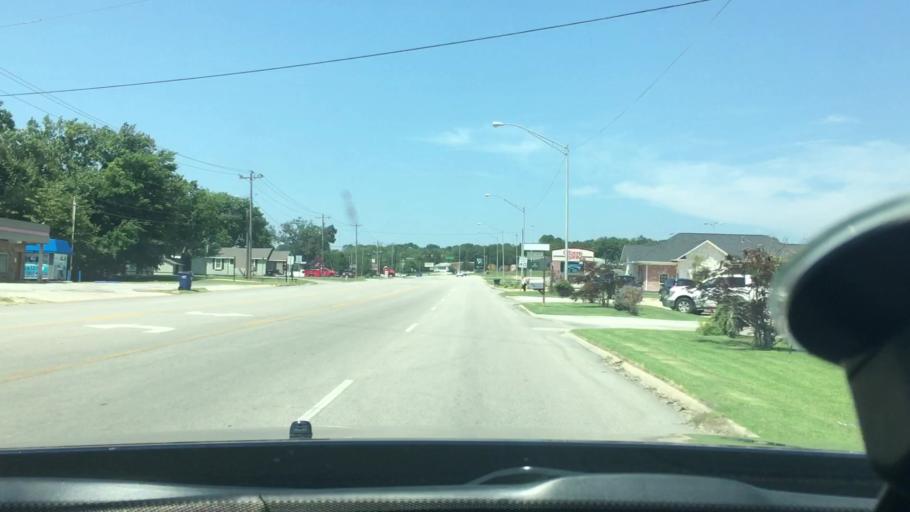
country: US
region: Oklahoma
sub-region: Pontotoc County
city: Ada
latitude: 34.7598
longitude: -96.6621
